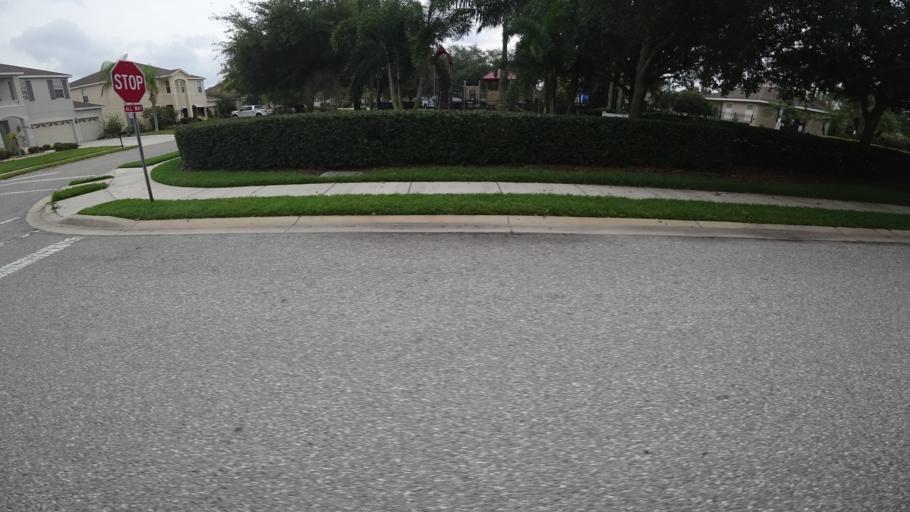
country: US
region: Florida
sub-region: Manatee County
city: Samoset
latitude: 27.4351
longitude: -82.5095
